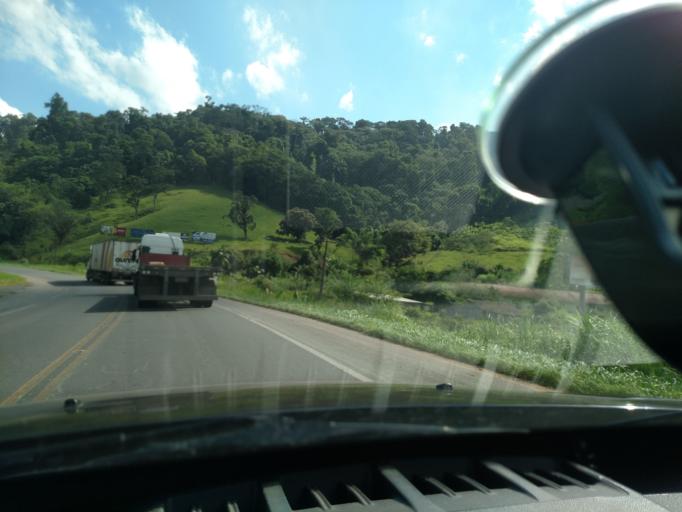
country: BR
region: Santa Catarina
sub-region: Rodeio
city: Gavea
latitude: -26.9507
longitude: -49.3261
